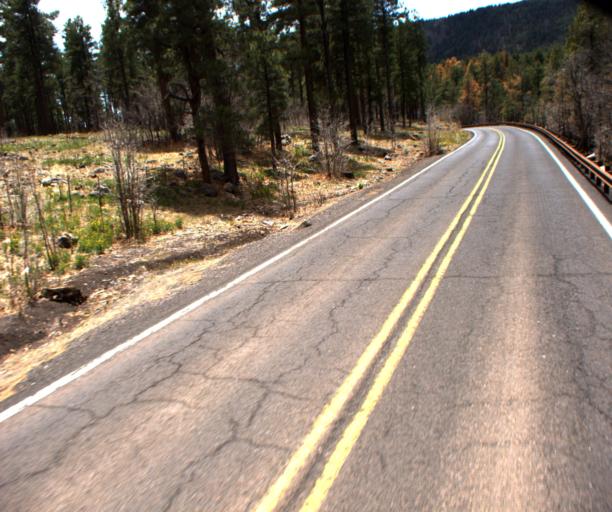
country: US
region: Arizona
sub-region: Coconino County
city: Kachina Village
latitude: 35.1000
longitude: -111.7314
